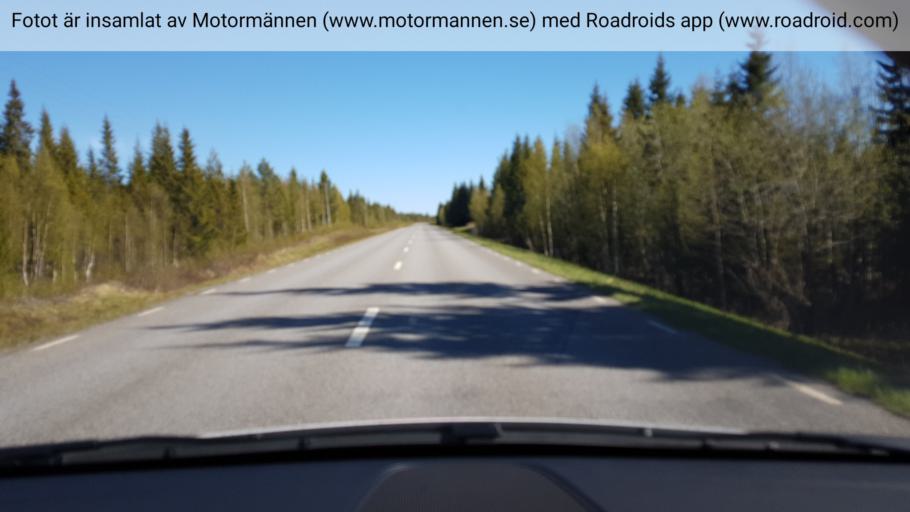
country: SE
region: Jaemtland
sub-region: Stroemsunds Kommun
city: Stroemsund
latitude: 64.2713
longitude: 15.3835
